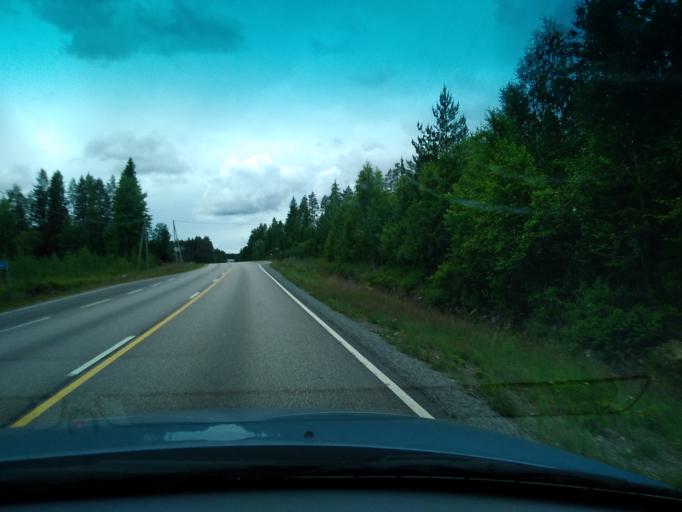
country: FI
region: Central Finland
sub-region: Saarijaervi-Viitasaari
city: Pylkoenmaeki
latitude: 62.6311
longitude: 24.8015
